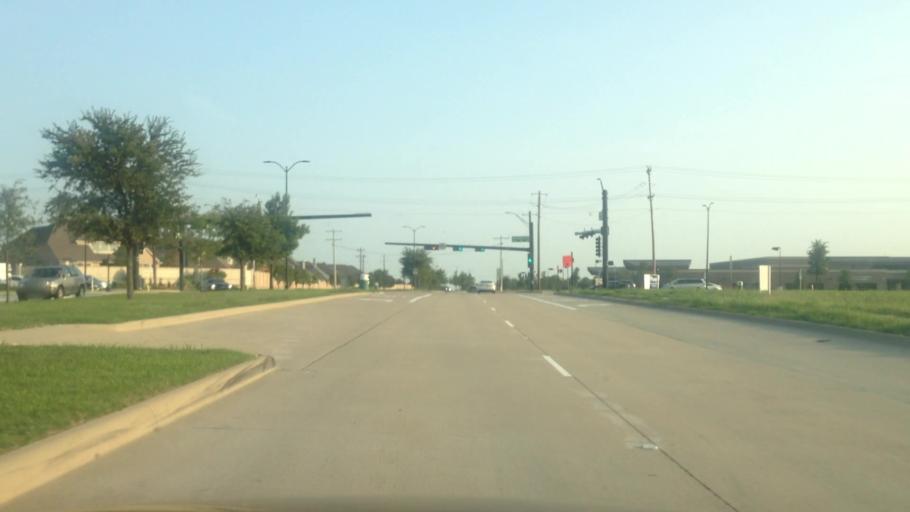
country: US
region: Texas
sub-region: Denton County
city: The Colony
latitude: 33.1340
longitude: -96.8693
